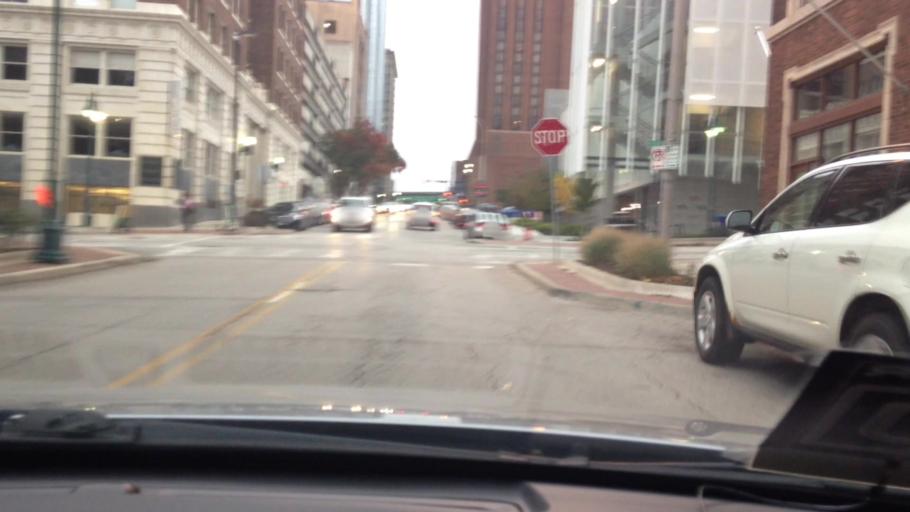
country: US
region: Missouri
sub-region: Jackson County
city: Kansas City
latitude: 39.1026
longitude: -94.5855
